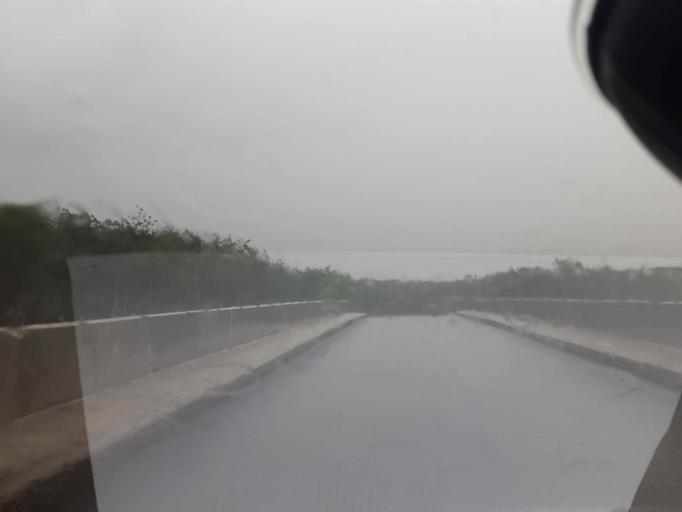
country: ID
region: Lampung
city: Kedaton
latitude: -5.3685
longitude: 105.3268
